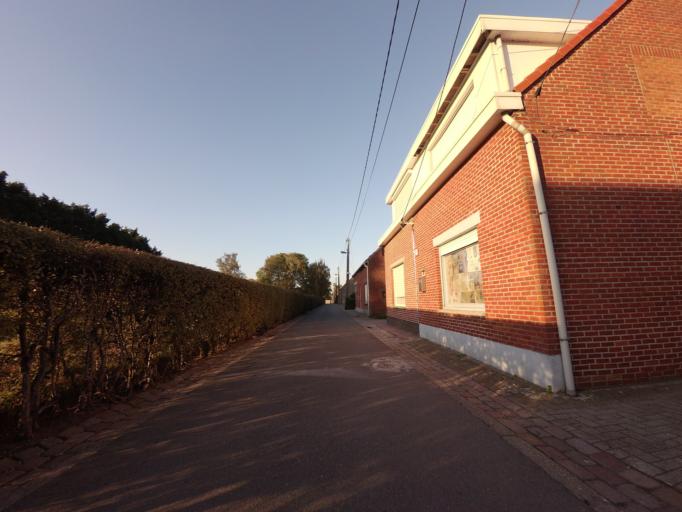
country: BE
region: Flanders
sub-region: Provincie Antwerpen
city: Stabroek
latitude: 51.3547
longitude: 4.3138
